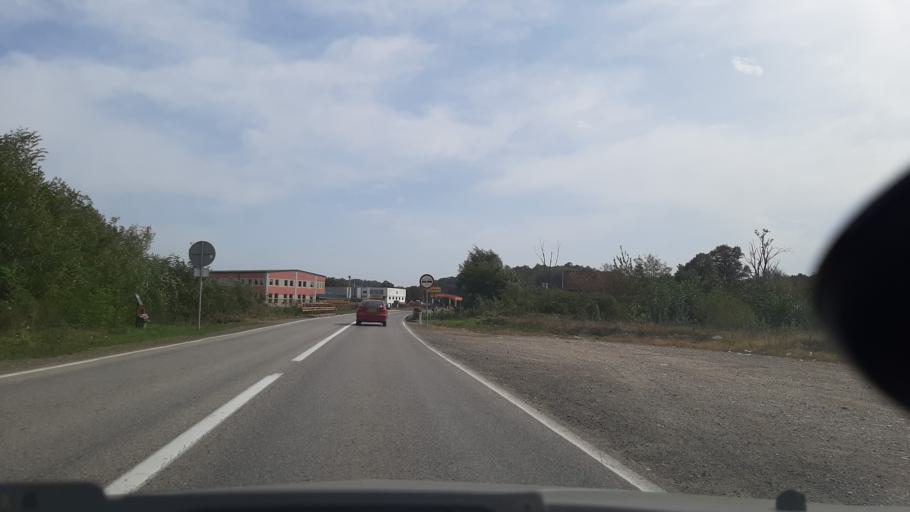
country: BA
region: Republika Srpska
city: Laktasi
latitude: 44.8767
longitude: 17.3072
